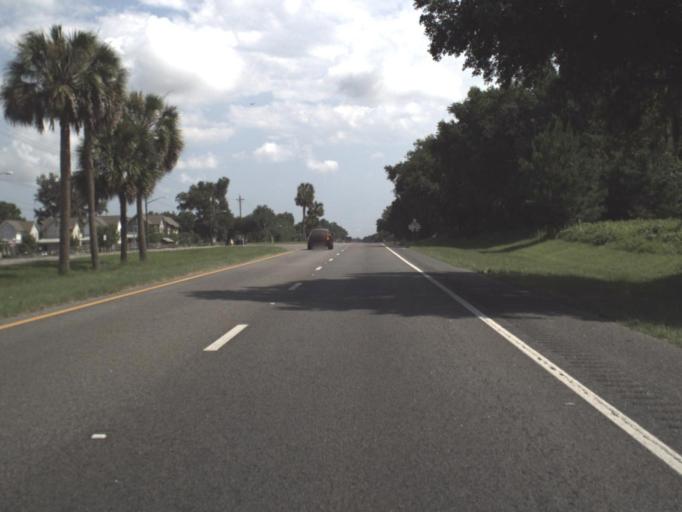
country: US
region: Florida
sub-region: Alachua County
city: Gainesville
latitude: 29.6075
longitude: -82.3418
